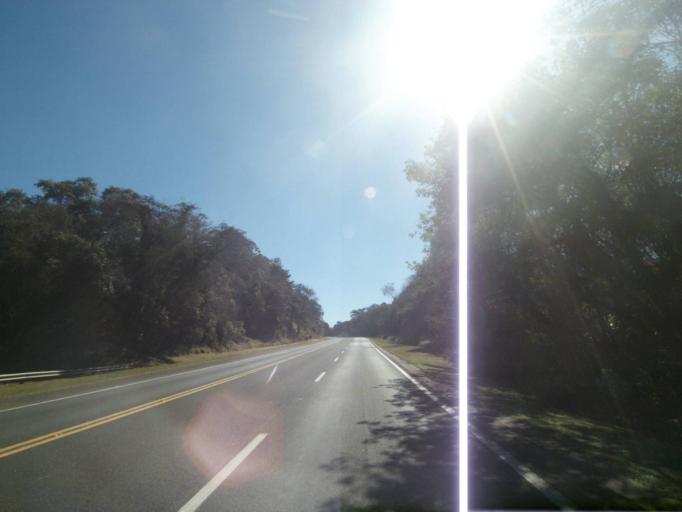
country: BR
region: Parana
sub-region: Reserva
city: Reserva
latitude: -24.6438
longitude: -50.6242
